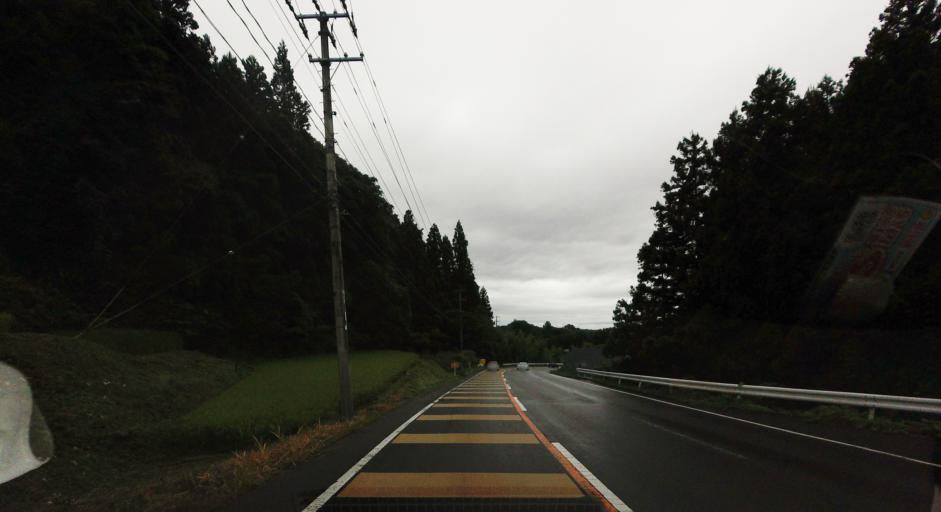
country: JP
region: Fukushima
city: Hobaramachi
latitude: 37.6705
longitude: 140.6364
